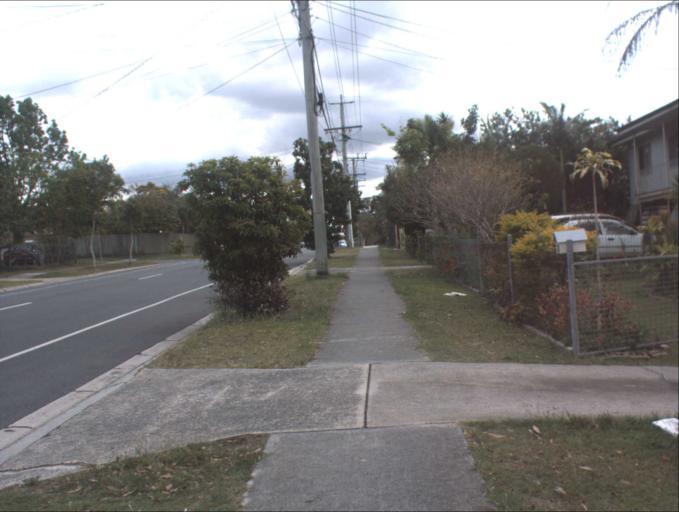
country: AU
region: Queensland
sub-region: Logan
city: Logan City
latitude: -27.6443
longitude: 153.1094
